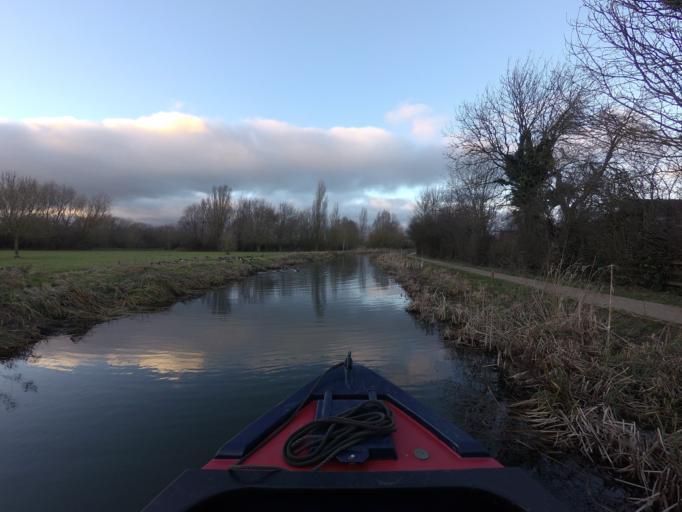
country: GB
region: England
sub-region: Northamptonshire
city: Blisworth
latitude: 52.2173
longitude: -0.9418
